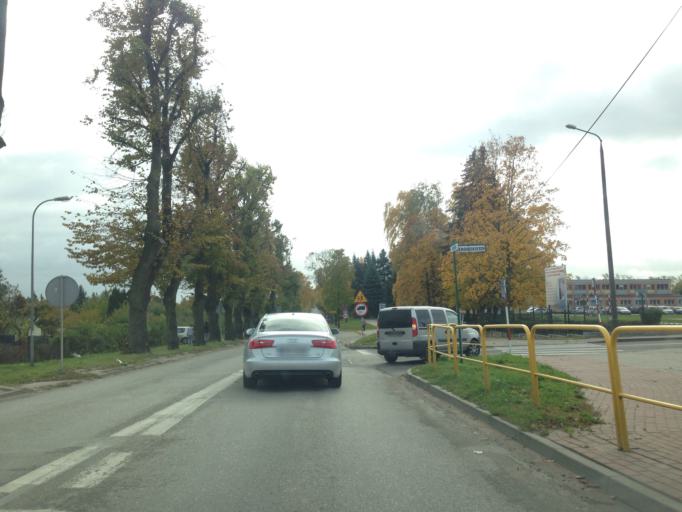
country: PL
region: Pomeranian Voivodeship
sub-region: Powiat tczewski
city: Tczew
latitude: 54.0764
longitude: 18.7934
